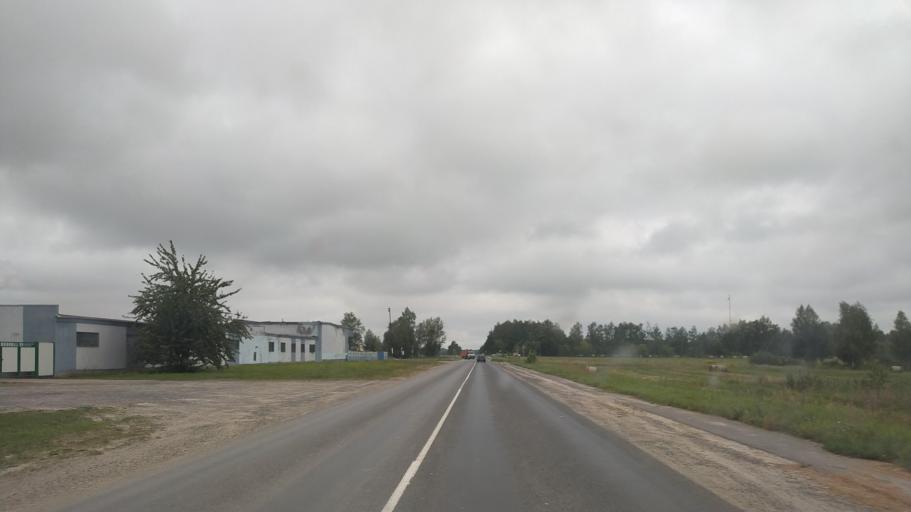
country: BY
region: Brest
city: Byaroza
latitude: 52.5519
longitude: 24.9346
